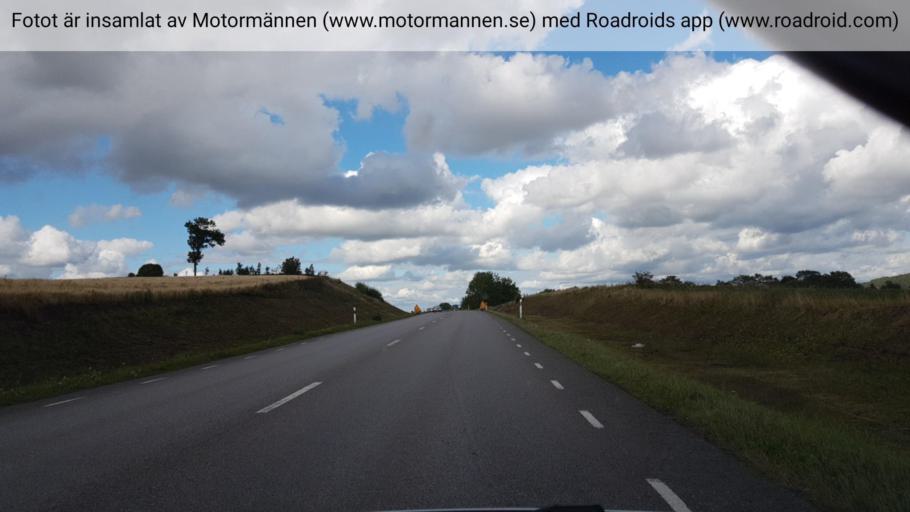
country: SE
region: Vaestra Goetaland
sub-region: Falkopings Kommun
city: Falkoeping
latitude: 58.1295
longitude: 13.5571
